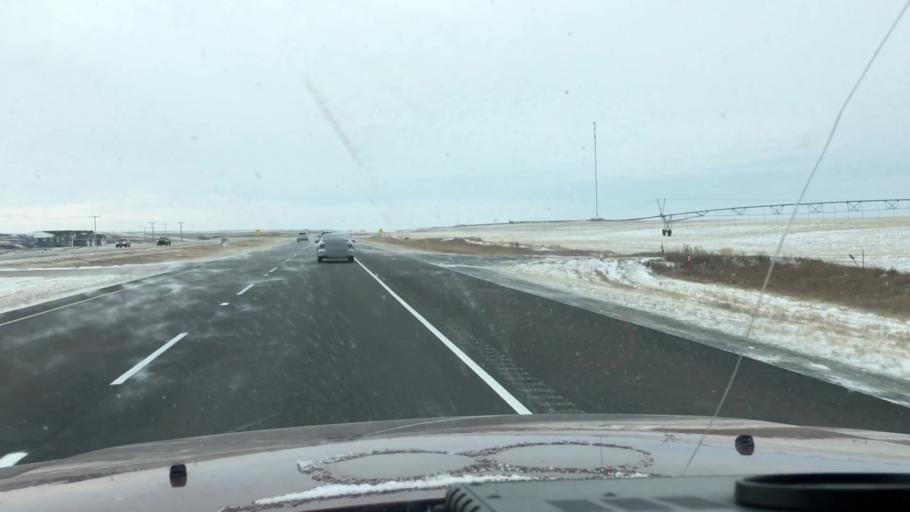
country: CA
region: Saskatchewan
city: Saskatoon
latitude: 51.7439
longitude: -106.4764
